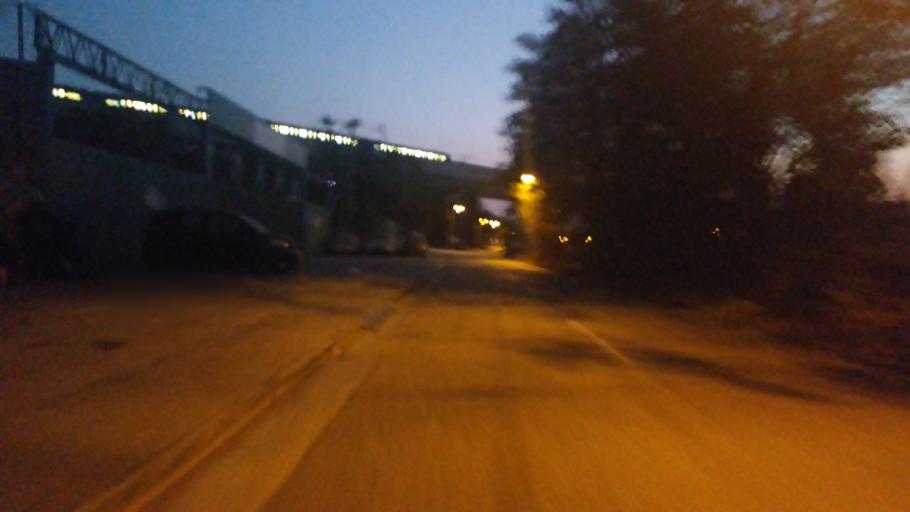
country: HK
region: Yuen Long
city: Yuen Long Kau Hui
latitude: 22.4439
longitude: 113.9967
